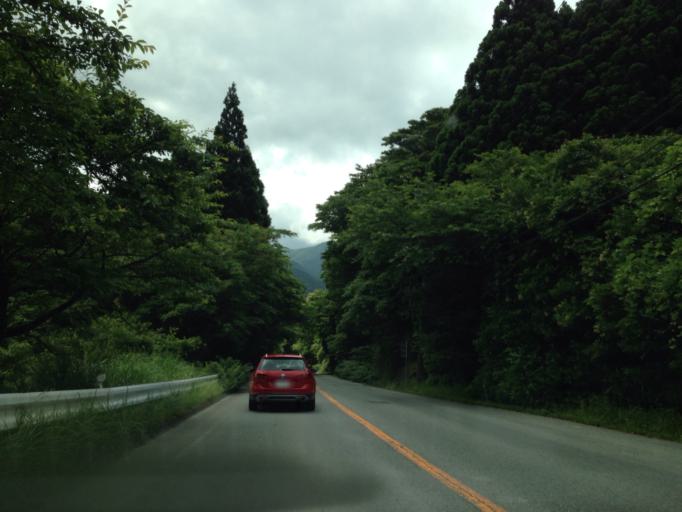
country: JP
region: Shizuoka
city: Heda
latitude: 34.9204
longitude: 138.8236
